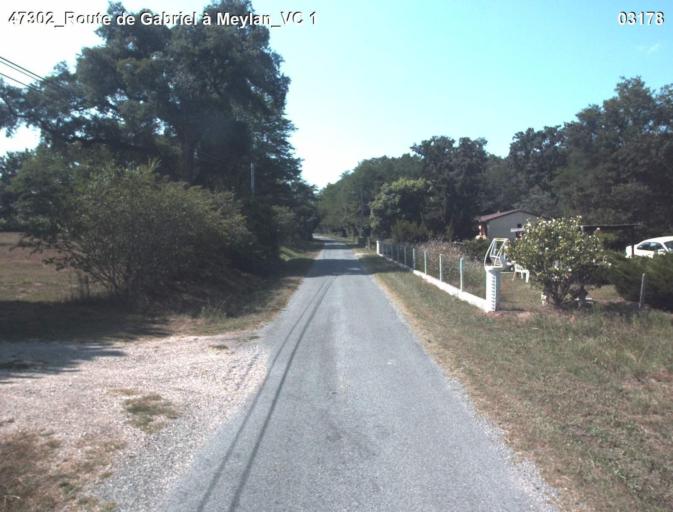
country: FR
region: Aquitaine
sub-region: Departement du Lot-et-Garonne
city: Mezin
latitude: 44.0731
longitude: 0.1251
